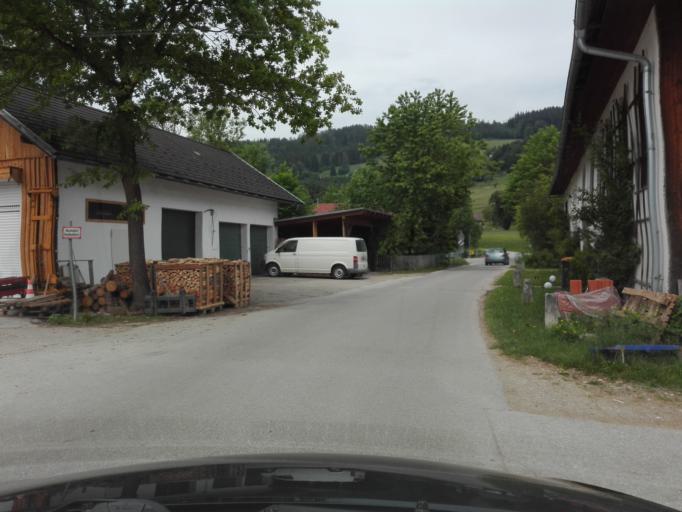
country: AT
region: Upper Austria
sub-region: Politischer Bezirk Gmunden
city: Scharnstein
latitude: 47.9104
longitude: 13.9512
